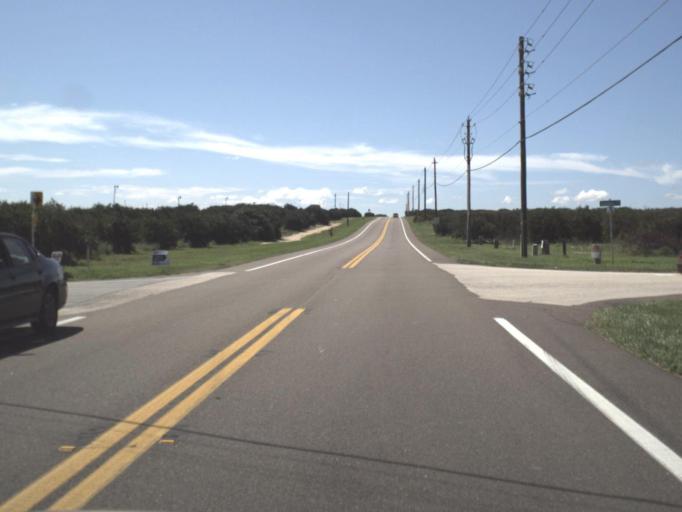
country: US
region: Florida
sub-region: Polk County
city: Auburndale
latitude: 28.1104
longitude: -81.7893
